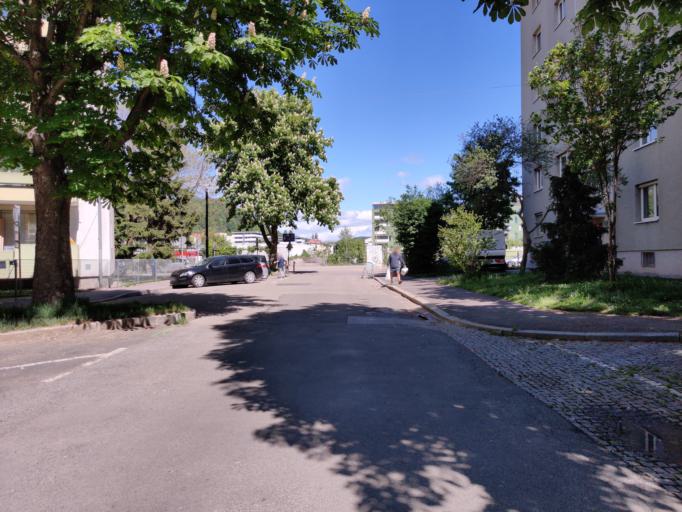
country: AT
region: Styria
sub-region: Graz Stadt
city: Wetzelsdorf
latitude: 47.0741
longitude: 15.4096
